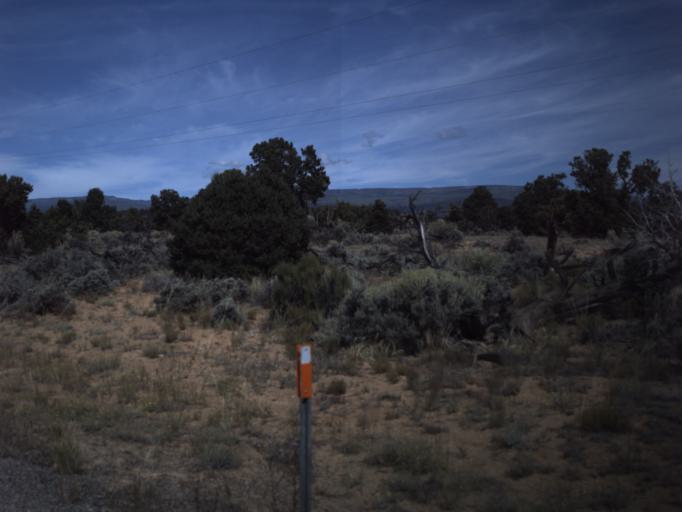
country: US
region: Utah
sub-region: Wayne County
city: Loa
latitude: 37.8585
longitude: -111.4358
